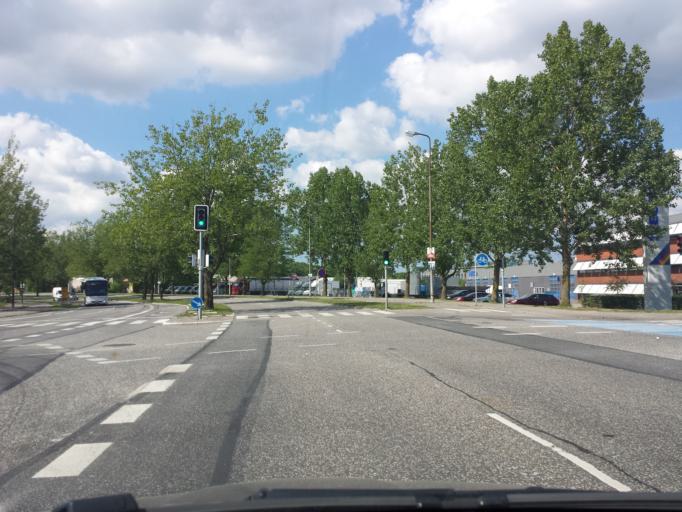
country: DK
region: Capital Region
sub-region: Herlev Kommune
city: Herlev
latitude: 55.6975
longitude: 12.4214
